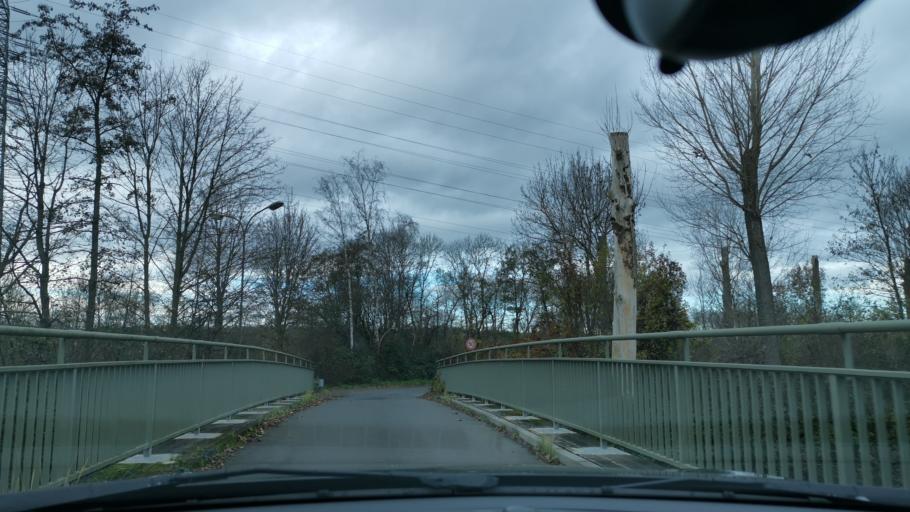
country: DE
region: North Rhine-Westphalia
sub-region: Regierungsbezirk Dusseldorf
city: Grevenbroich
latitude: 51.0523
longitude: 6.5693
